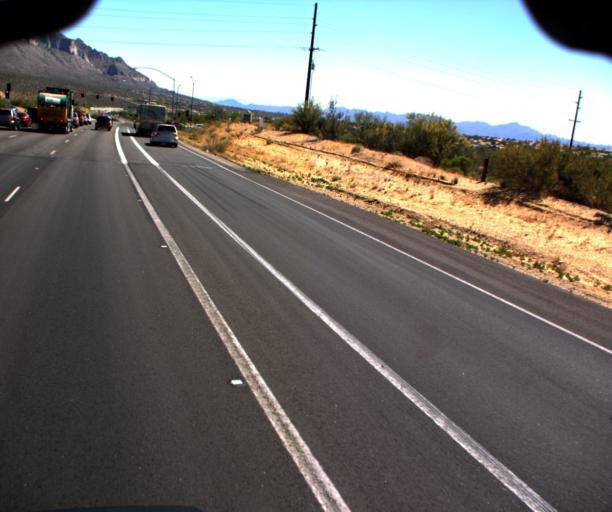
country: US
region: Arizona
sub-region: Pima County
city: Oro Valley
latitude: 32.4282
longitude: -110.9347
